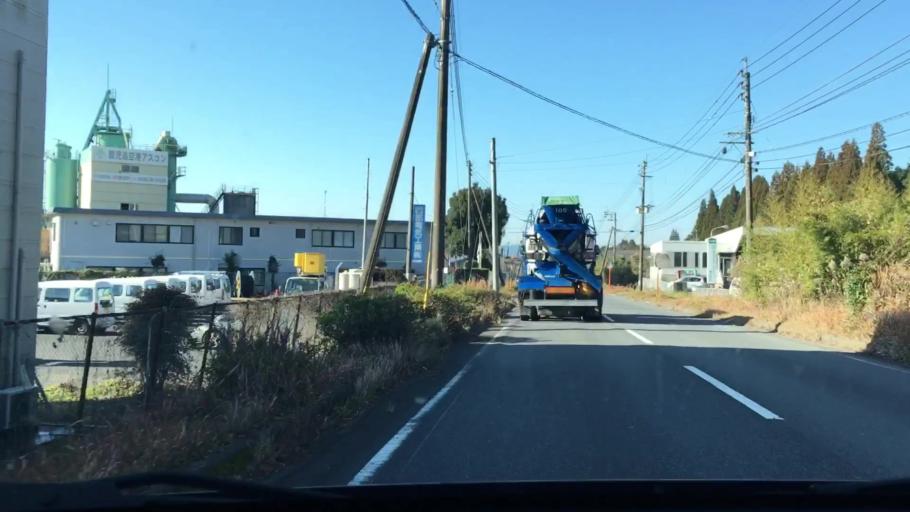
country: JP
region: Kagoshima
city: Kajiki
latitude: 31.7717
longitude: 130.6961
